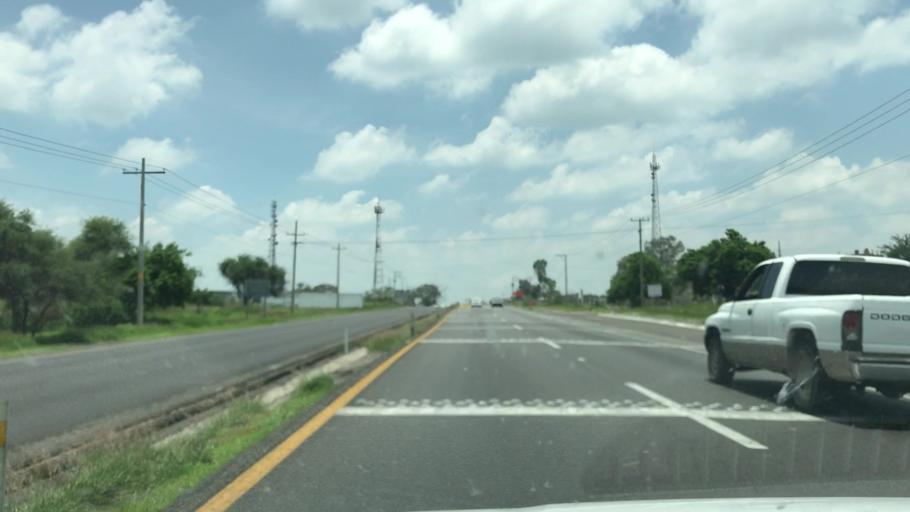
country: MX
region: Guanajuato
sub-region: Irapuato
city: San Ignacio de Rivera (Ojo de Agua)
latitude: 20.5600
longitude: -101.4494
